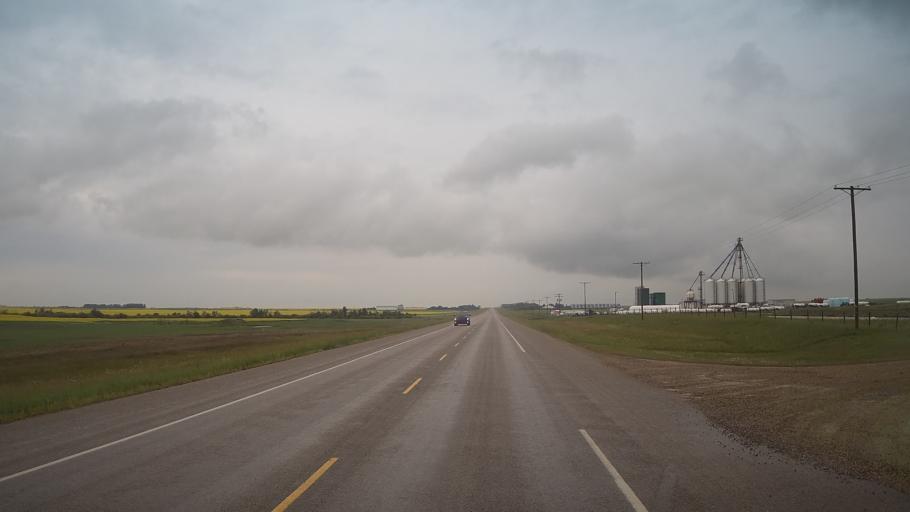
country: CA
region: Saskatchewan
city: Wilkie
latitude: 52.4057
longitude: -108.7526
